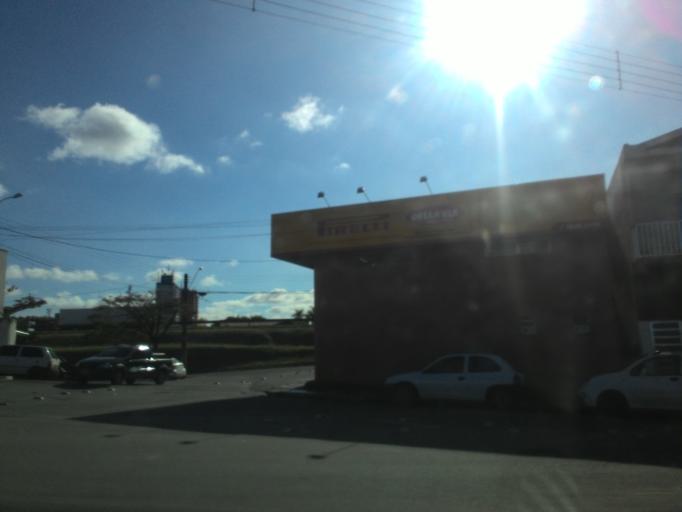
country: BR
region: Sao Paulo
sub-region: Registro
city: Registro
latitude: -24.4969
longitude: -47.8403
